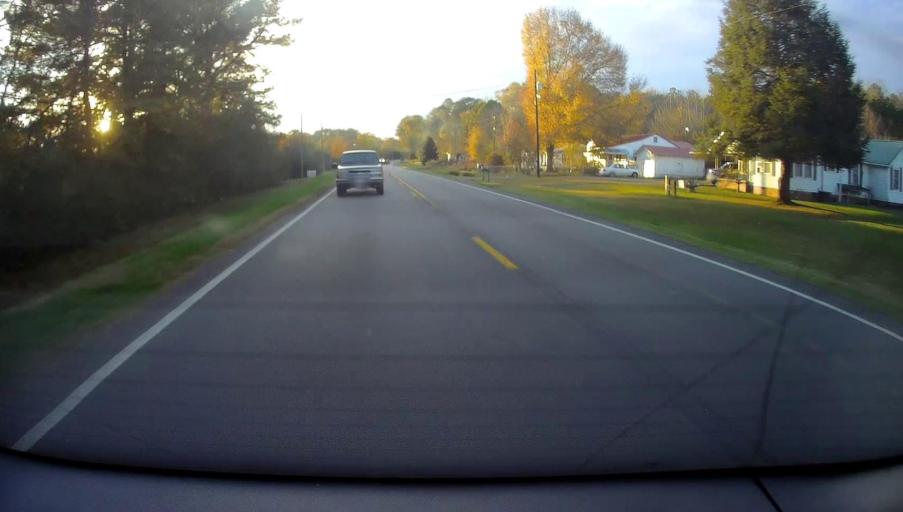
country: US
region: Alabama
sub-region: Etowah County
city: Attalla
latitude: 34.0399
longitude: -86.1372
